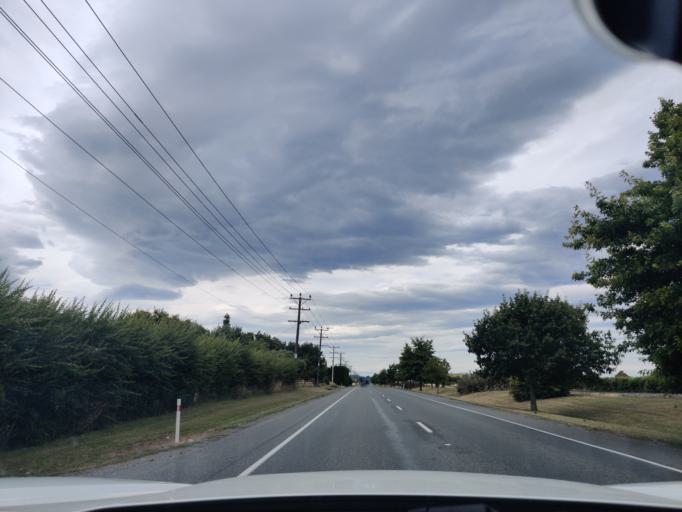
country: NZ
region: Wellington
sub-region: Masterton District
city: Masterton
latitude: -40.9573
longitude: 175.6162
